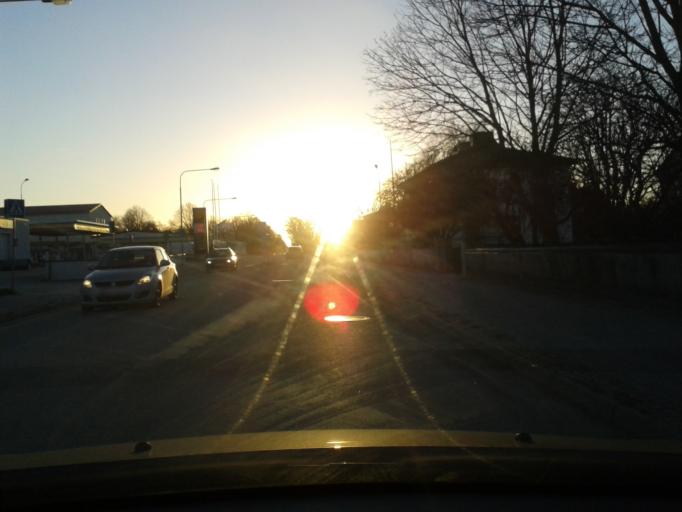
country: SE
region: Gotland
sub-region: Gotland
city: Visby
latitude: 57.6304
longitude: 18.2868
